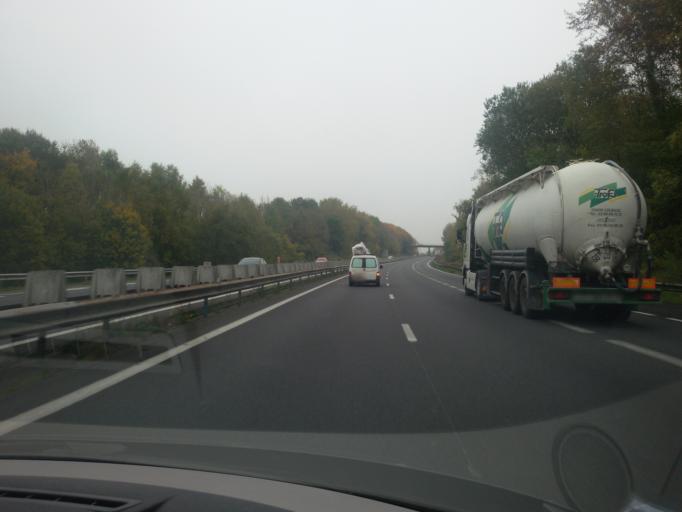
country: FR
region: Lower Normandy
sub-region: Departement du Calvados
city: Blonville-sur-Mer
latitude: 49.2484
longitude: 0.0592
